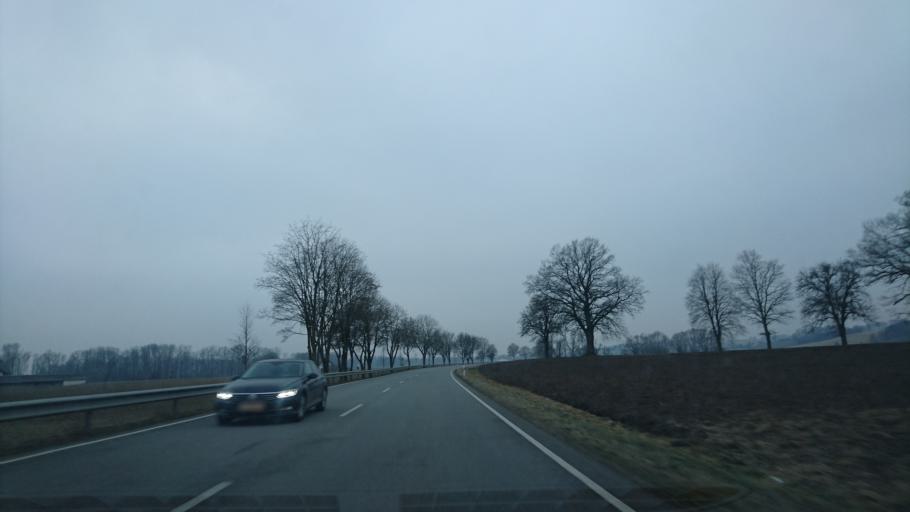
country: DE
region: Bavaria
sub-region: Lower Bavaria
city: Pocking
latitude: 48.4267
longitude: 13.3199
